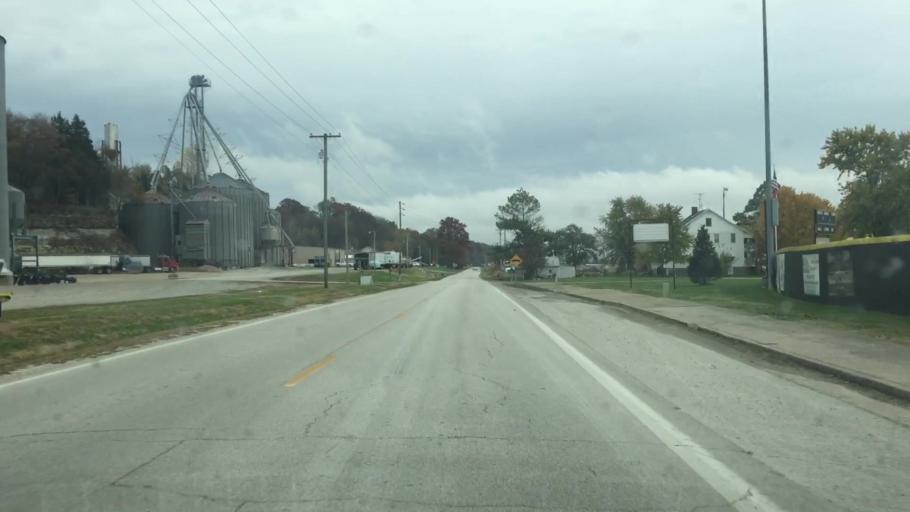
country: US
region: Missouri
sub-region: Gasconade County
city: Hermann
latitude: 38.7182
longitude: -91.5171
